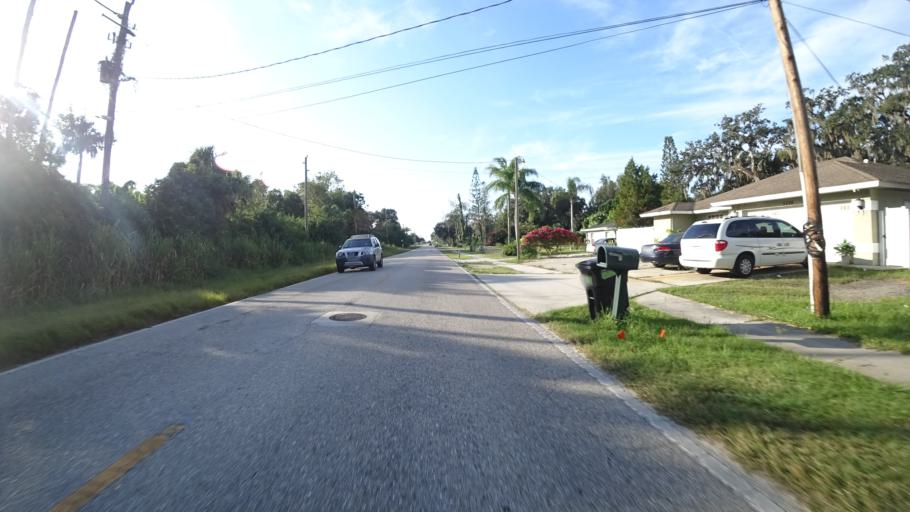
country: US
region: Florida
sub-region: Manatee County
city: Samoset
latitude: 27.4704
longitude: -82.5302
